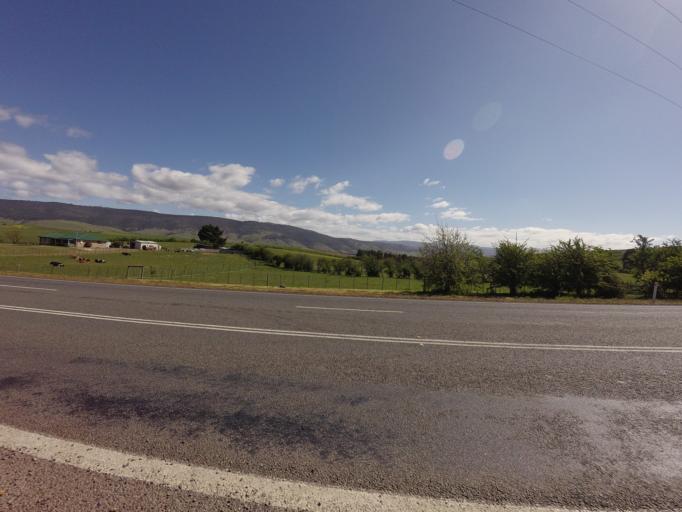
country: AU
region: Tasmania
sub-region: Derwent Valley
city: New Norfolk
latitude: -42.7176
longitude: 146.9481
